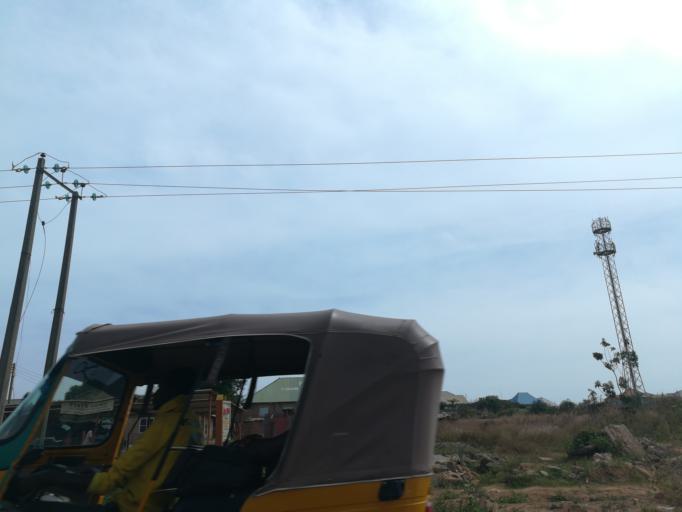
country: NG
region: Plateau
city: Jos
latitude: 9.8855
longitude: 8.8651
